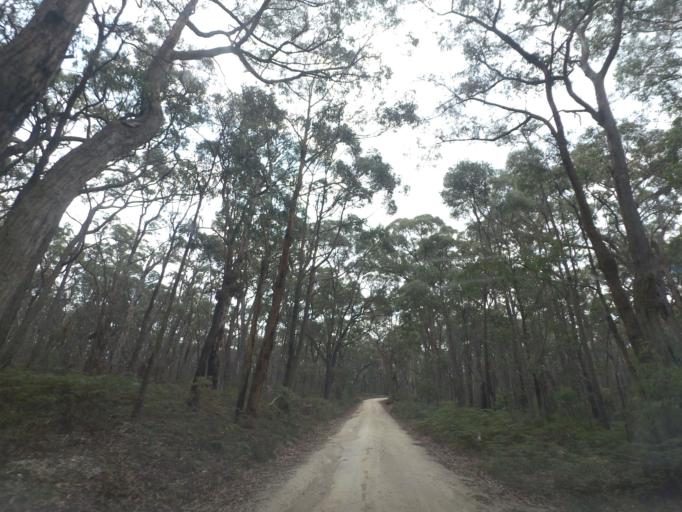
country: AU
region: Victoria
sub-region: Moorabool
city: Bacchus Marsh
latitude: -37.5083
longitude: 144.4284
